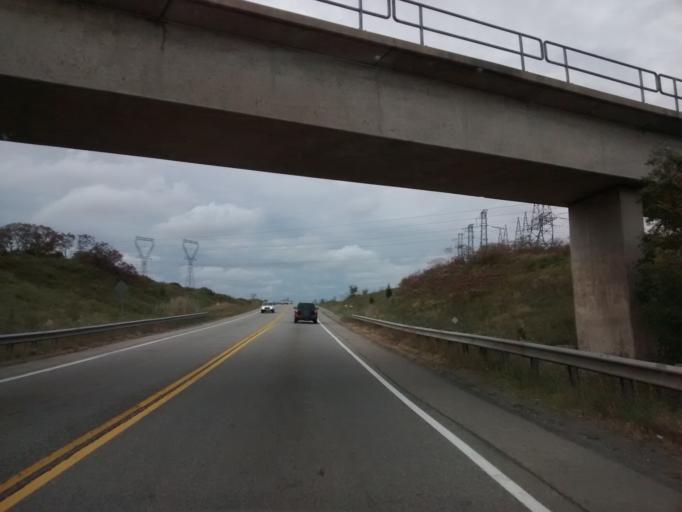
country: CA
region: Ontario
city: Ancaster
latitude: 43.0843
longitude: -79.9641
